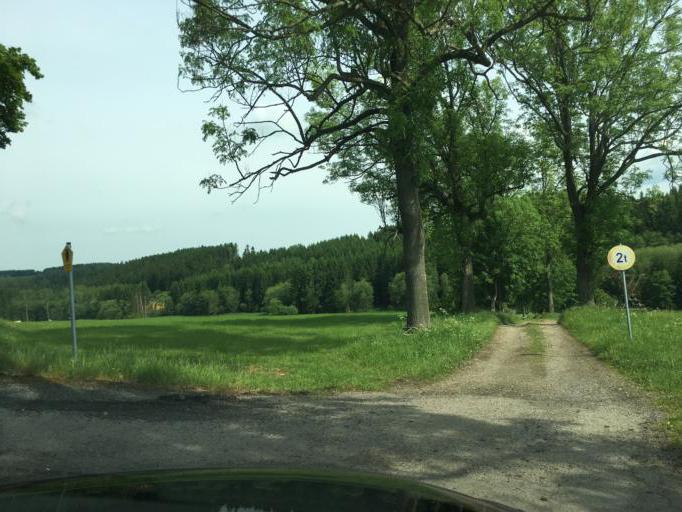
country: DE
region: Saxony
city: Frauenstein
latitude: 50.7779
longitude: 13.5563
